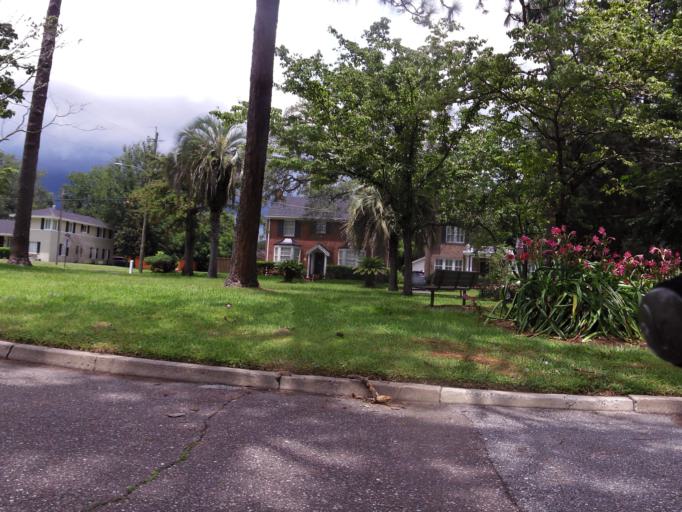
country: US
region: Florida
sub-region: Duval County
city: Jacksonville
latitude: 30.3047
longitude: -81.7028
